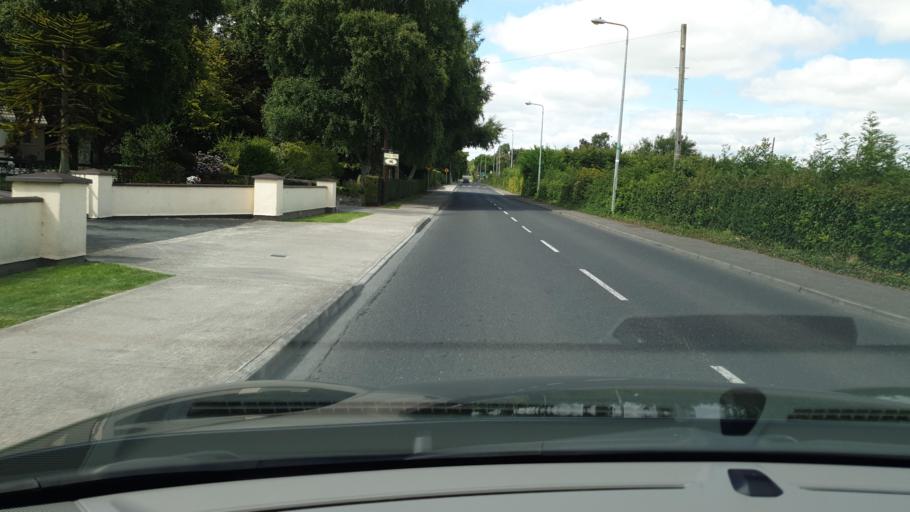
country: IE
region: Leinster
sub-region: An Mhi
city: Ratoath
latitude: 53.5099
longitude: -6.4633
